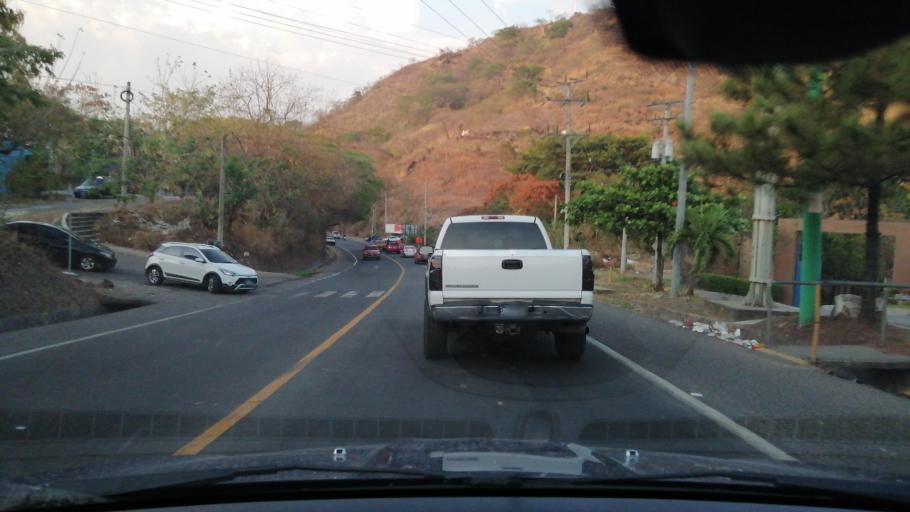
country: SV
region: Santa Ana
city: Santa Ana
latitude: 13.9897
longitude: -89.5427
